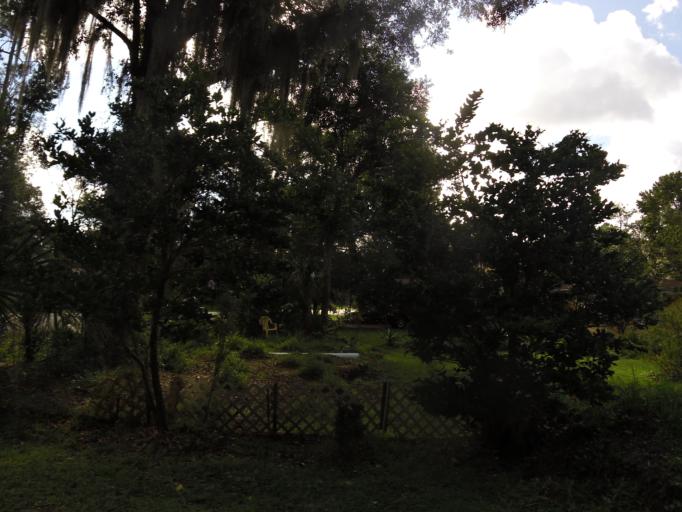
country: US
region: Georgia
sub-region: Camden County
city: Kingsland
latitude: 30.8038
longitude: -81.6946
